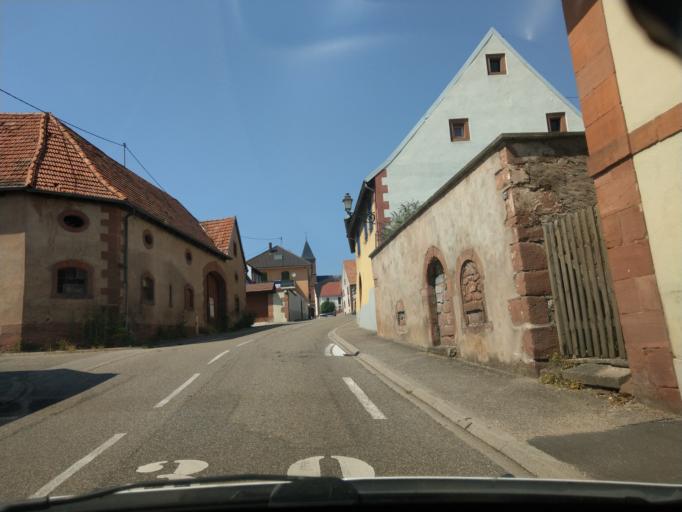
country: FR
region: Alsace
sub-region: Departement du Bas-Rhin
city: Dossenheim-sur-Zinsel
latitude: 48.8038
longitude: 7.4027
